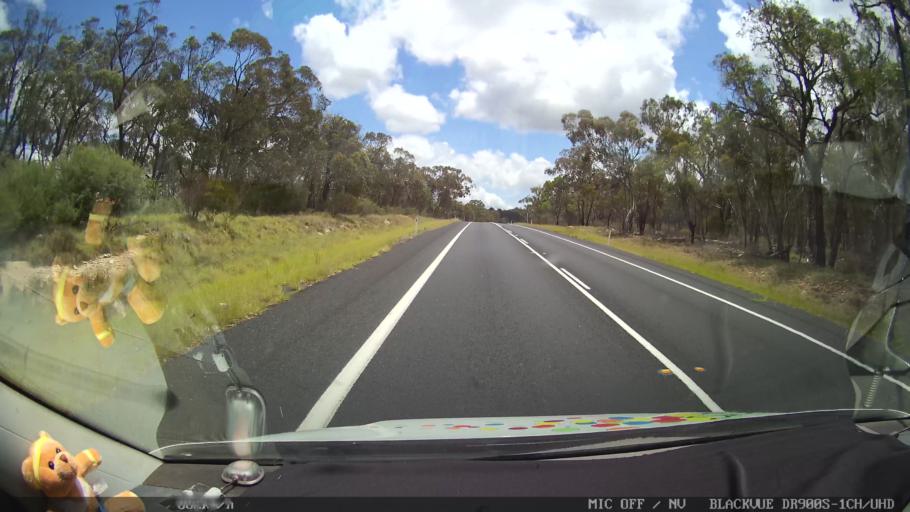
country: AU
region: New South Wales
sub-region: Glen Innes Severn
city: Glen Innes
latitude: -29.3589
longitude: 151.8983
